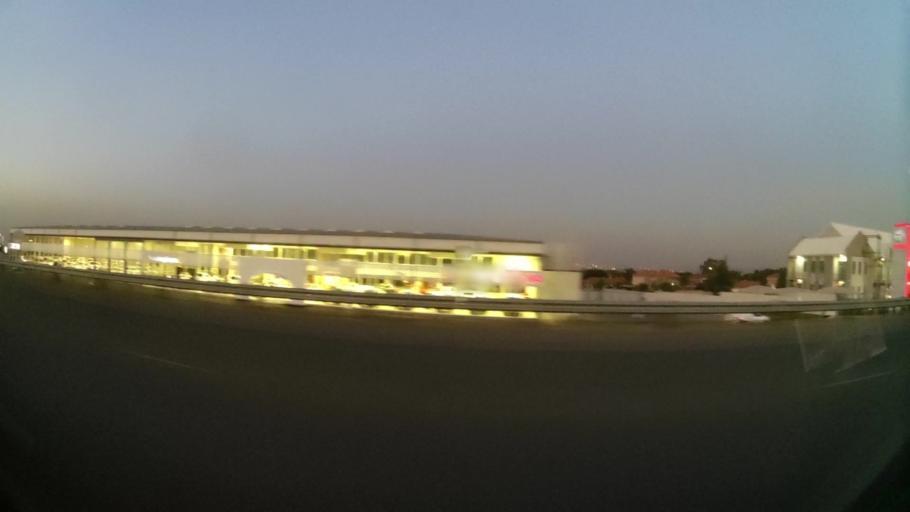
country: ZA
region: North-West
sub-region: Bojanala Platinum District Municipality
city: Rustenburg
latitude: -25.6916
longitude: 27.2535
